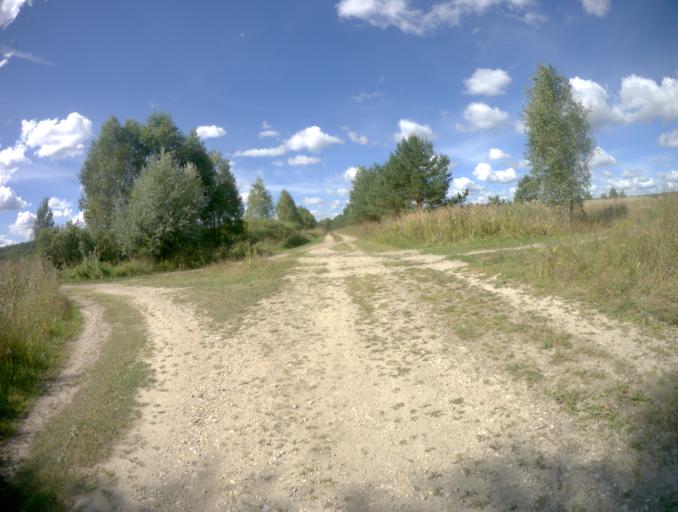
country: RU
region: Vladimir
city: Nikologory
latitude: 56.0084
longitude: 41.8865
